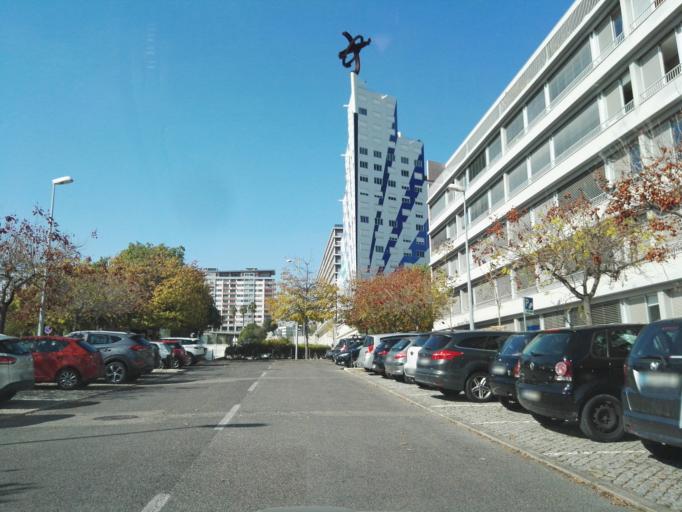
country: PT
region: Lisbon
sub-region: Loures
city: Moscavide
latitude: 38.7546
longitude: -9.0960
